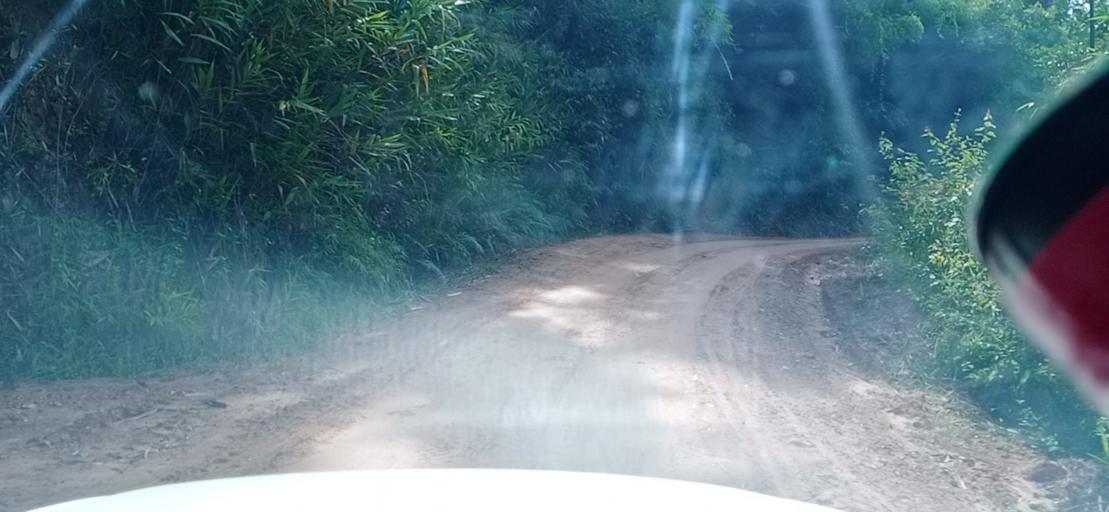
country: TH
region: Changwat Bueng Kan
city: Pak Khat
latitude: 18.6393
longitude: 103.2447
